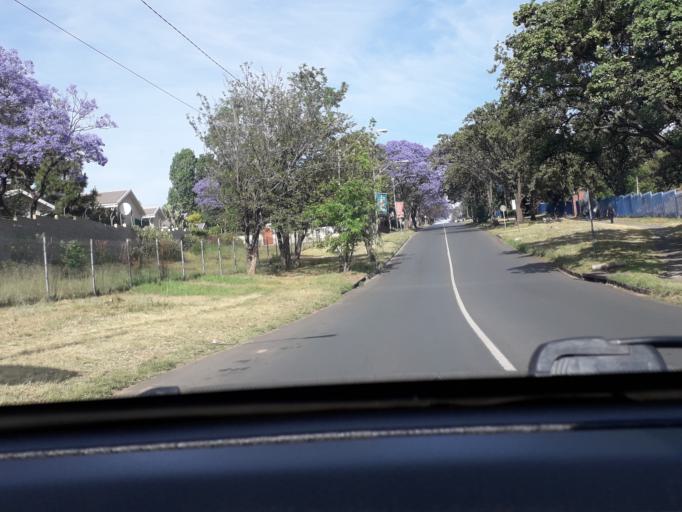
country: ZA
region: Gauteng
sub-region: City of Johannesburg Metropolitan Municipality
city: Johannesburg
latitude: -26.1381
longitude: 28.0948
